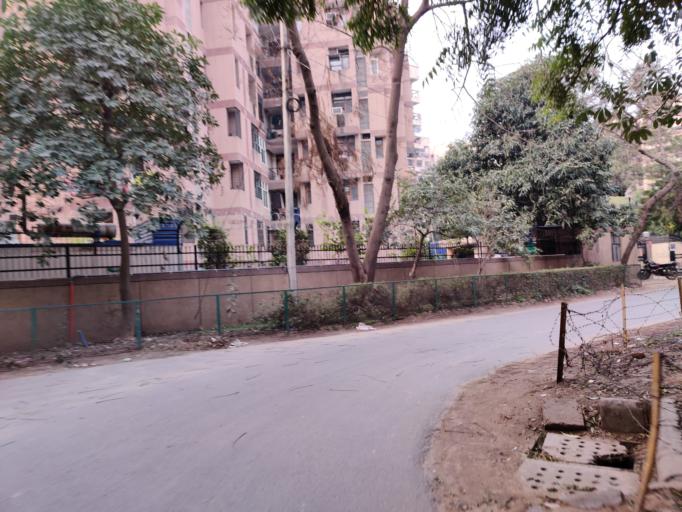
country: IN
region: Haryana
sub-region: Gurgaon
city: Gurgaon
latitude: 28.4423
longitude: 77.0633
